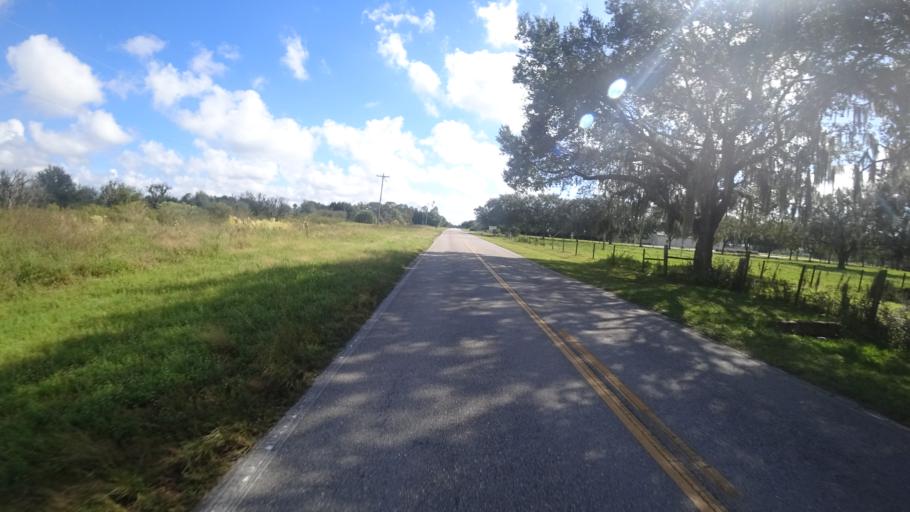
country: US
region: Florida
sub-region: Sarasota County
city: Lake Sarasota
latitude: 27.3393
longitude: -82.2006
